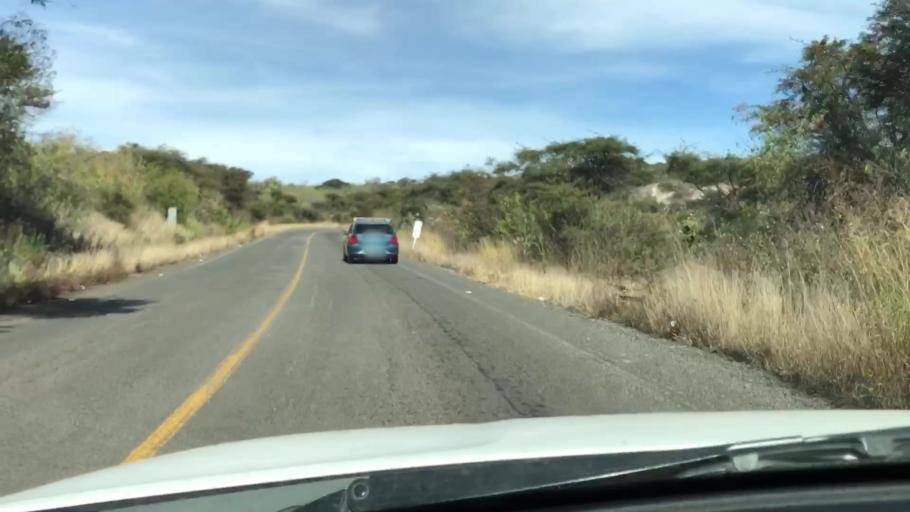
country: MX
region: Jalisco
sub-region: Zacoalco de Torres
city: Barranca de Otates (Barranca de Otatan)
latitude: 20.1914
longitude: -103.7006
